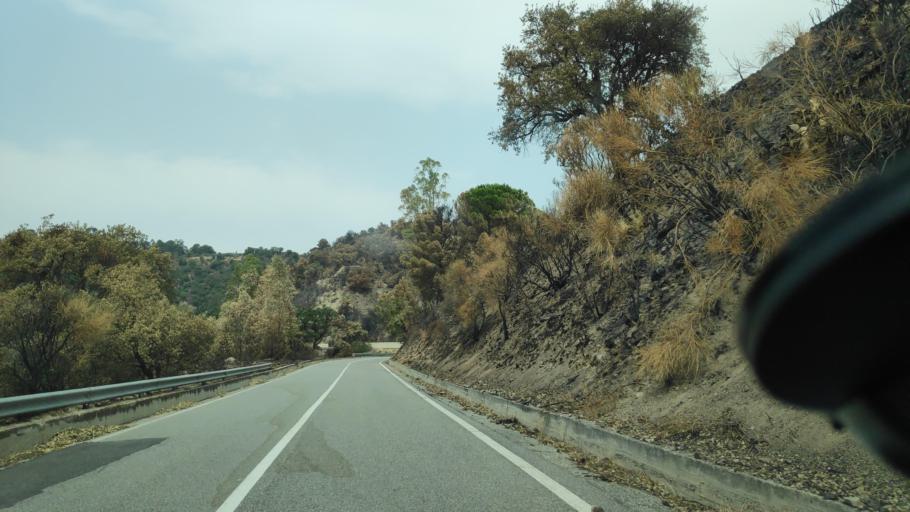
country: IT
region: Calabria
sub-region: Provincia di Catanzaro
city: Sant'Andrea Apostolo dello Ionio
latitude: 38.6410
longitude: 16.5188
